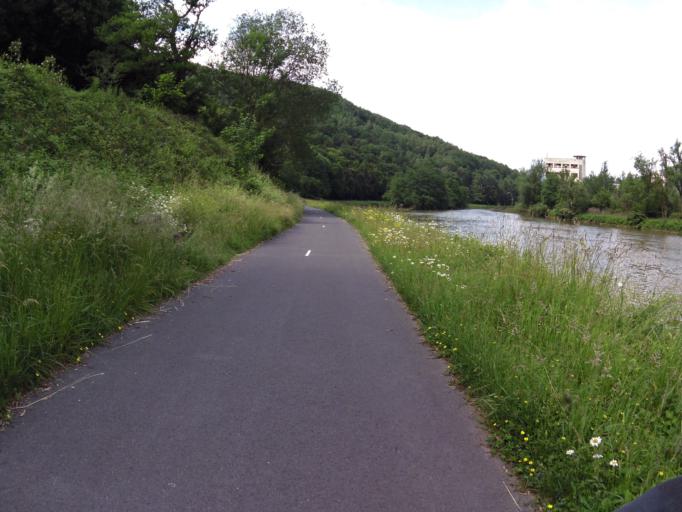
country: FR
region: Champagne-Ardenne
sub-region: Departement des Ardennes
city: Montherme
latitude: 49.8590
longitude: 4.7346
